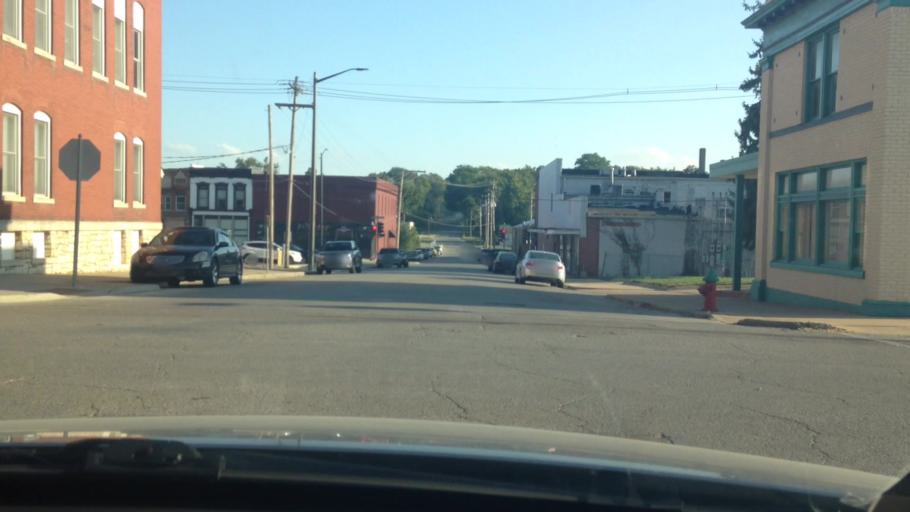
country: US
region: Kansas
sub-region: Leavenworth County
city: Leavenworth
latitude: 39.3178
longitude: -94.9170
